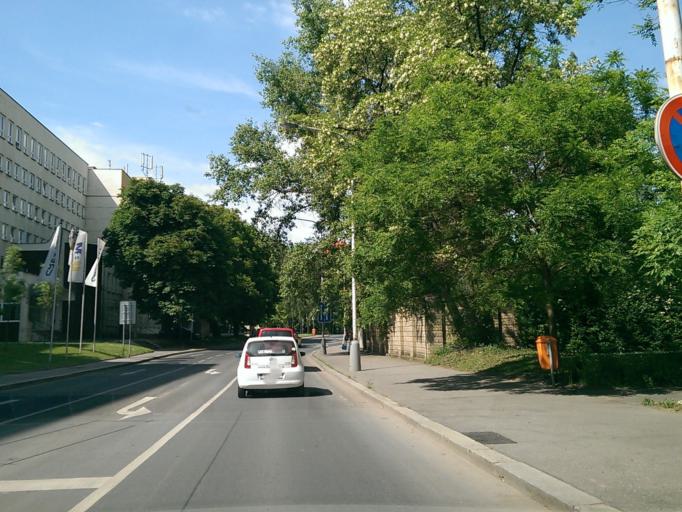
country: CZ
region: Praha
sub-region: Praha 8
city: Liben
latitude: 50.1056
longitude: 14.4706
